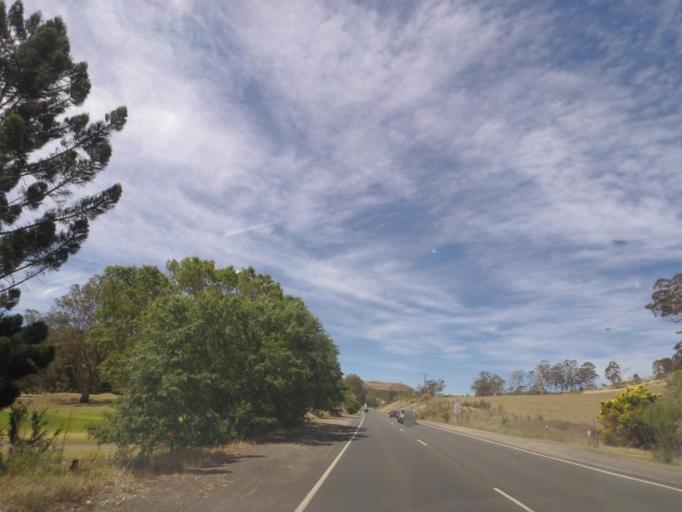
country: AU
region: New South Wales
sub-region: Wollondilly
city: Picton
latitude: -34.1659
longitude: 150.6309
